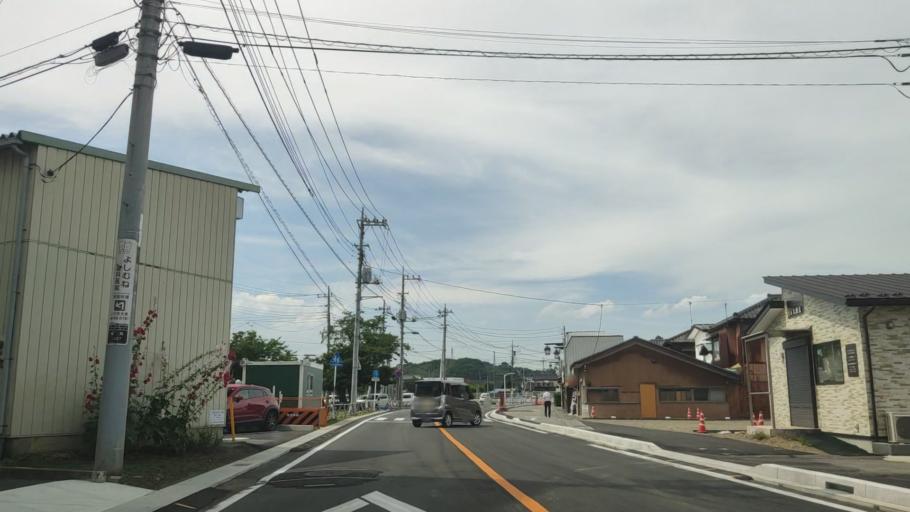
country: JP
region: Gunma
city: Tomioka
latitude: 36.2588
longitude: 138.8913
